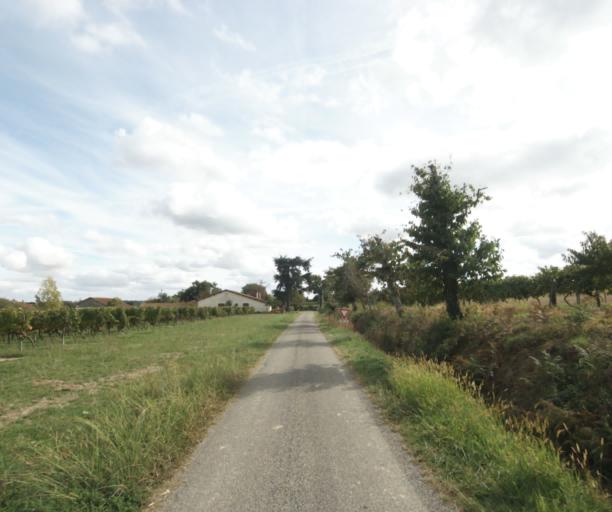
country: FR
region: Midi-Pyrenees
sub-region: Departement du Gers
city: Eauze
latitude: 43.8155
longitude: 0.1413
